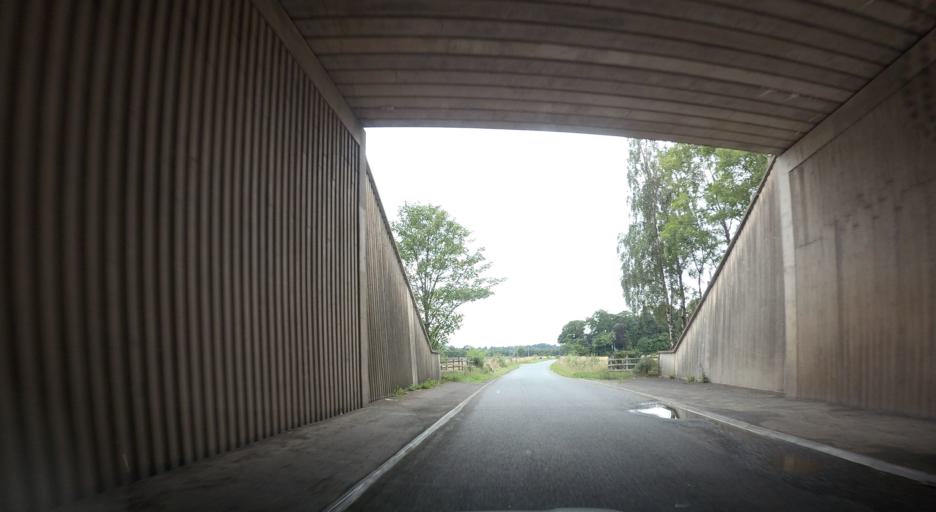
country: GB
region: Scotland
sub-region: Perth and Kinross
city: Bridge of Earn
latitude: 56.3535
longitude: -3.3996
